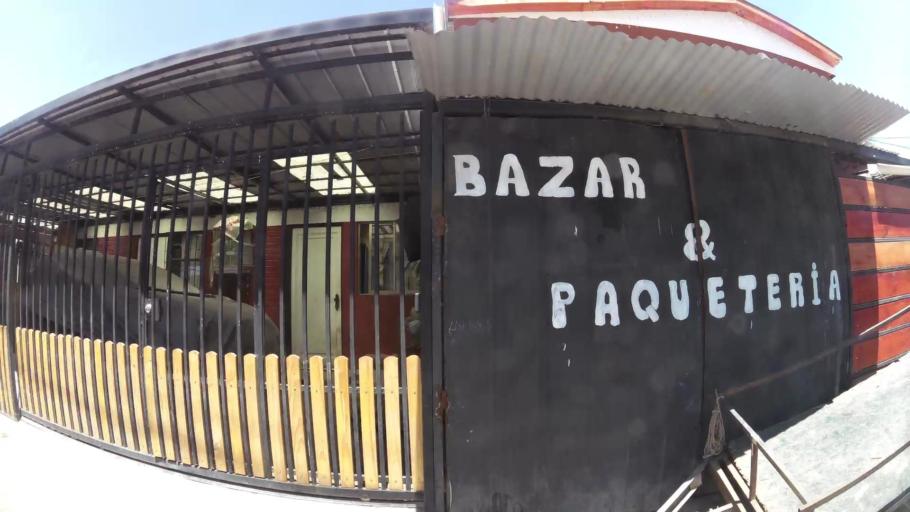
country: CL
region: Santiago Metropolitan
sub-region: Provincia de Maipo
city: San Bernardo
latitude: -33.5838
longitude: -70.6681
